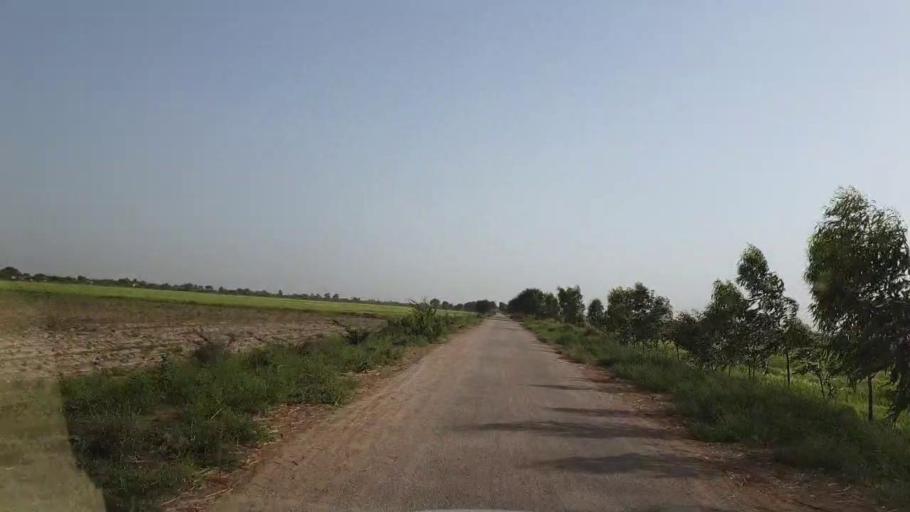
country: PK
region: Sindh
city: Tando Ghulam Ali
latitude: 25.0916
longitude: 68.8530
